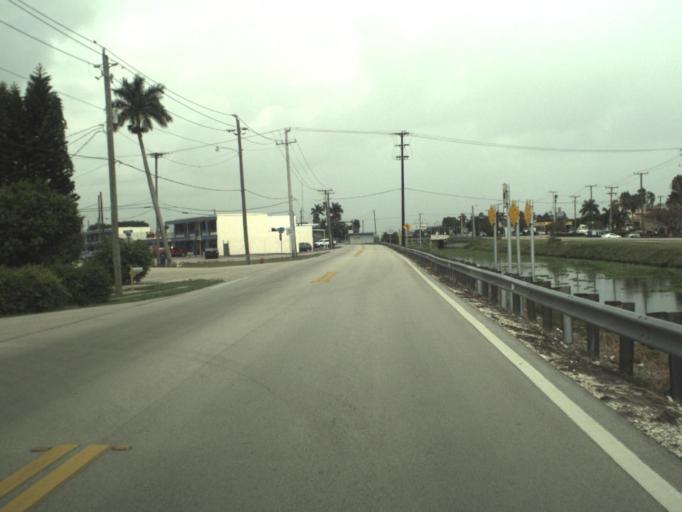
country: US
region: Florida
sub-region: Palm Beach County
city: Belle Glade
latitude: 26.6847
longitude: -80.6651
